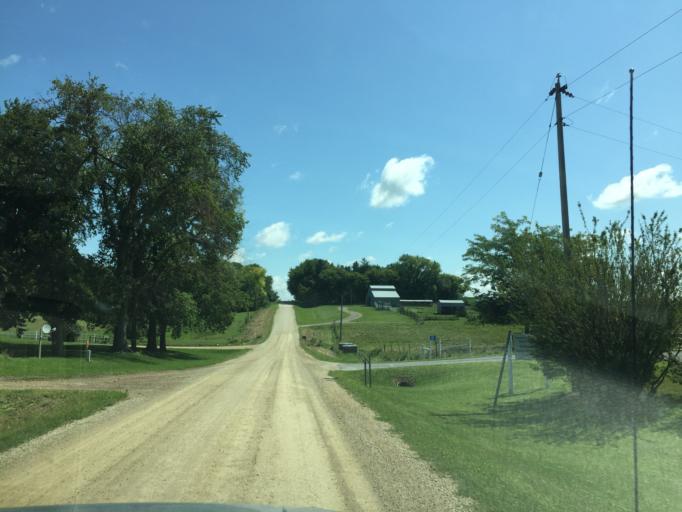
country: US
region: Minnesota
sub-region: Olmsted County
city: Byron
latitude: 44.0218
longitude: -92.6544
